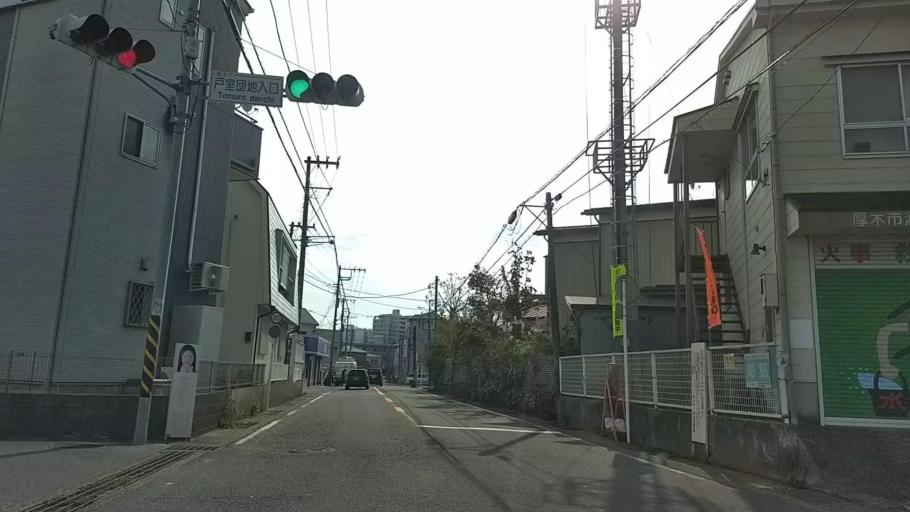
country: JP
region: Kanagawa
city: Atsugi
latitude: 35.4480
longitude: 139.3527
